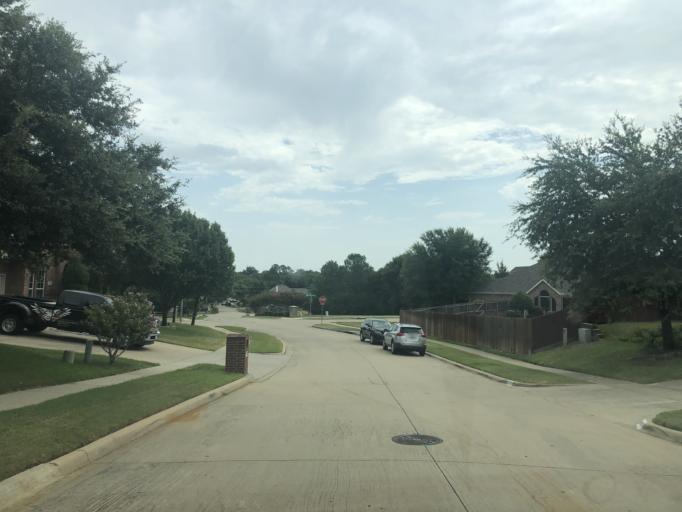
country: US
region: Texas
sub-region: Dallas County
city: Grand Prairie
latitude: 32.7652
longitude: -97.0393
